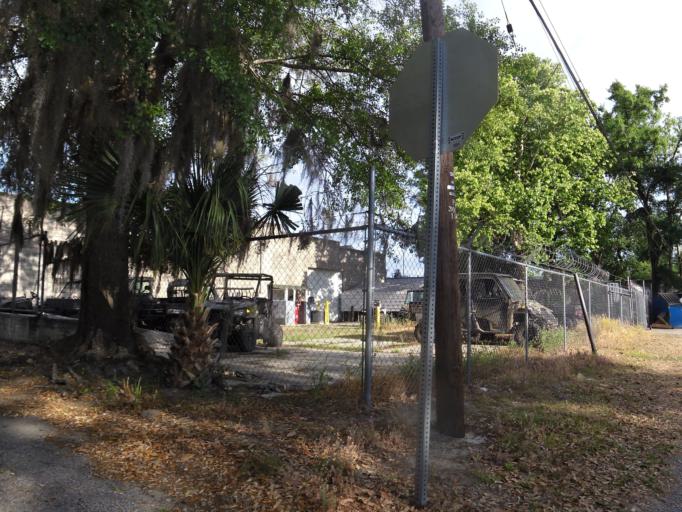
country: US
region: South Carolina
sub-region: Hampton County
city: Estill
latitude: 32.7552
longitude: -81.2428
